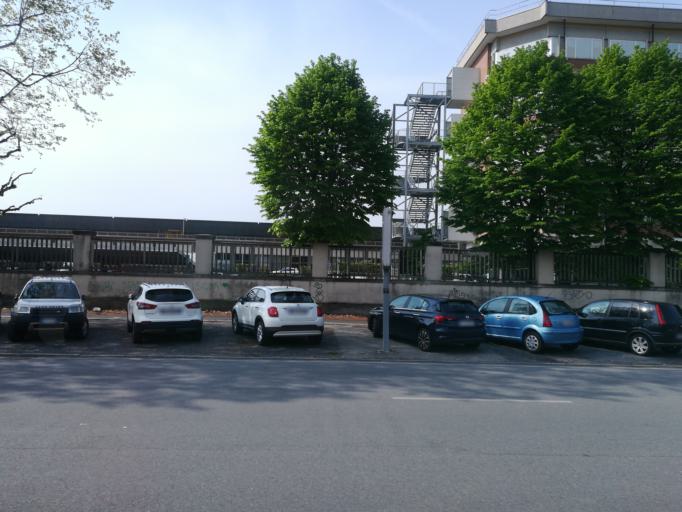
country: IT
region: Piedmont
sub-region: Provincia di Torino
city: Gerbido
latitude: 45.0287
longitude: 7.6195
